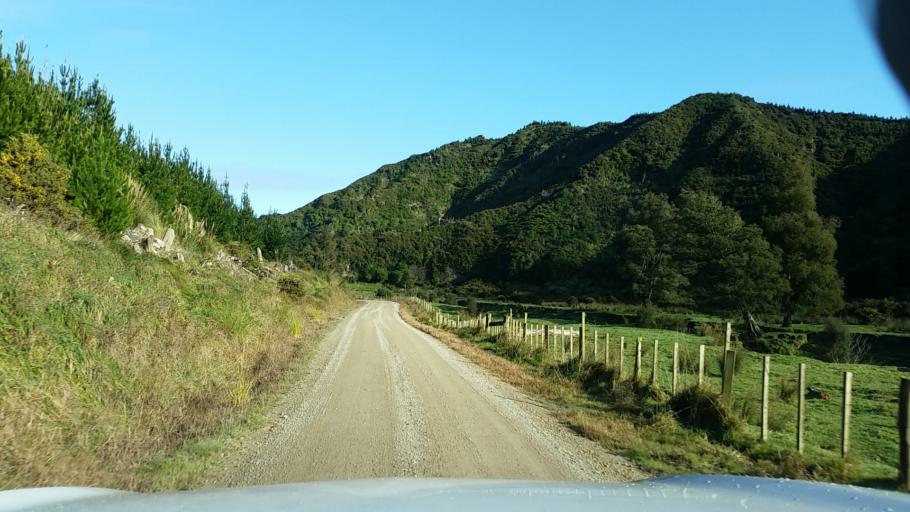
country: NZ
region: Taranaki
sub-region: South Taranaki District
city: Patea
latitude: -39.6927
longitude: 174.7504
